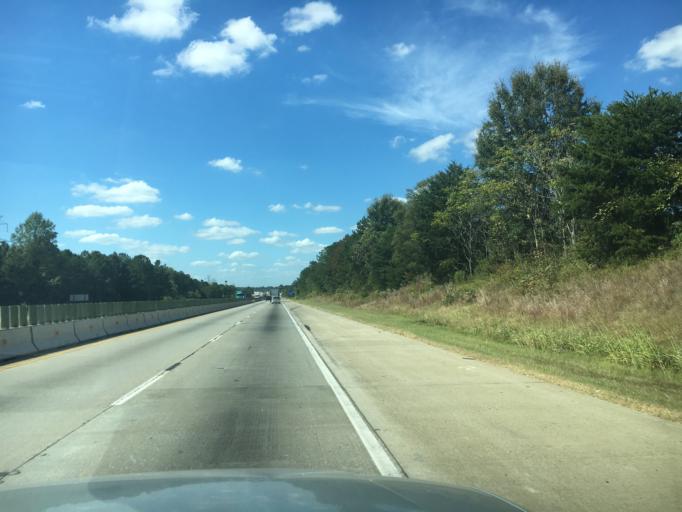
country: US
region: South Carolina
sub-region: Spartanburg County
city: Valley Falls
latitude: 35.0124
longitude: -81.9396
